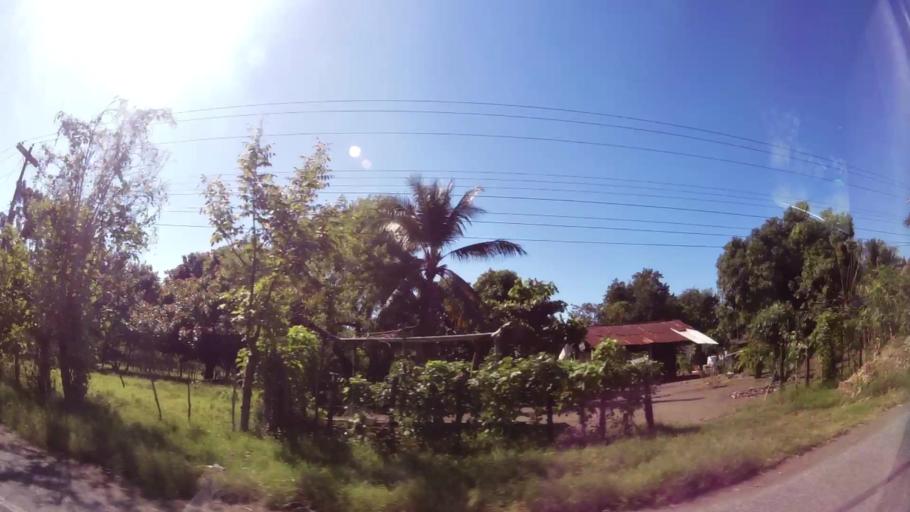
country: GT
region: Santa Rosa
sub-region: Municipio de Taxisco
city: Taxisco
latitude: 13.9101
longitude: -90.5266
